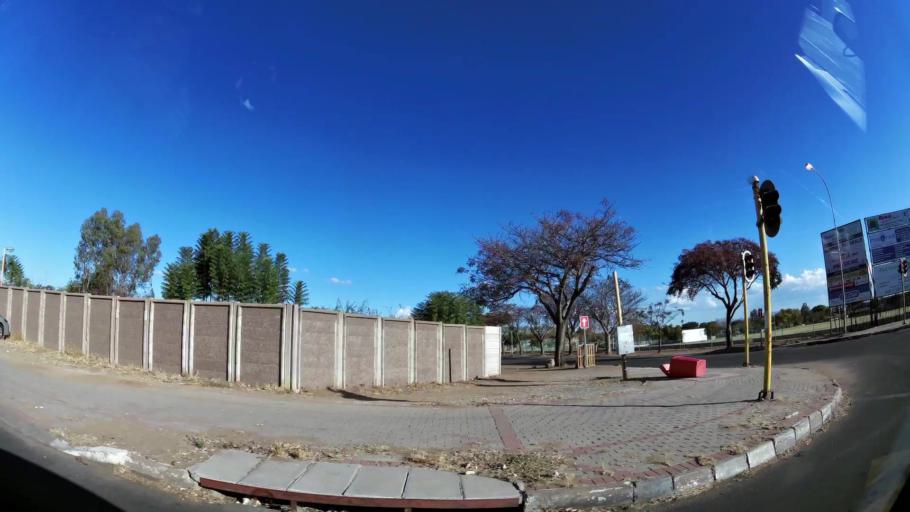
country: ZA
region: Limpopo
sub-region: Capricorn District Municipality
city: Polokwane
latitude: -23.8970
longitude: 29.4571
